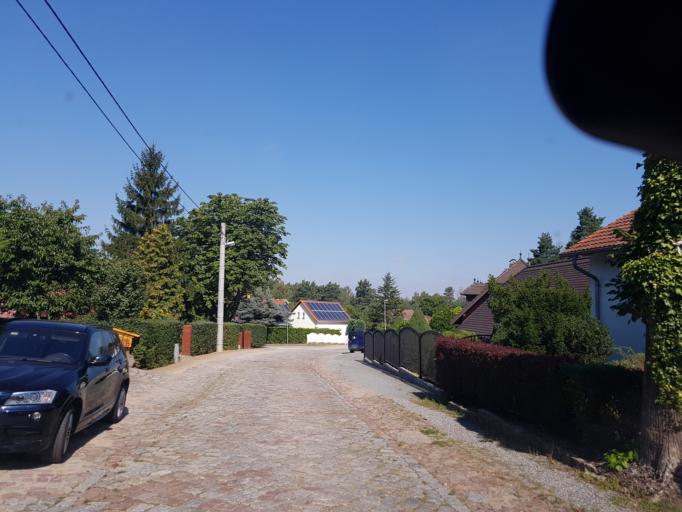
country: DE
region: Brandenburg
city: Elsterwerda
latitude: 51.4972
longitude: 13.5025
